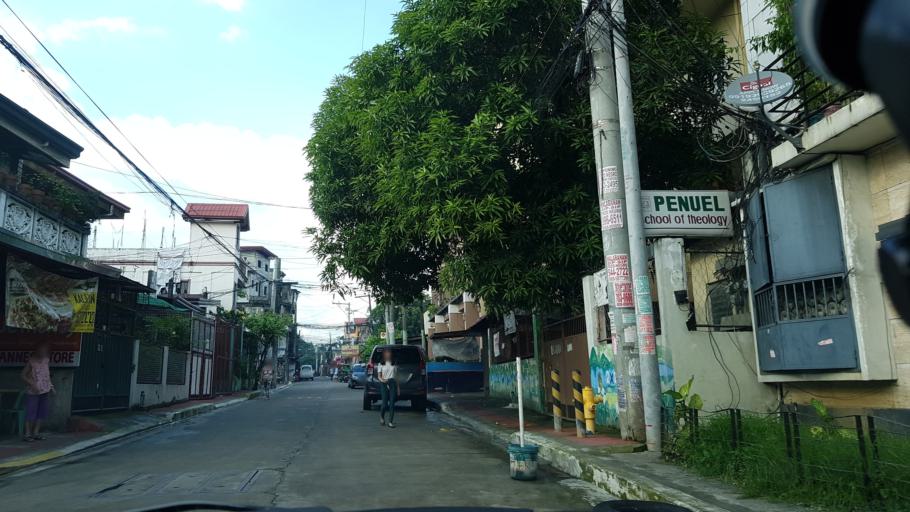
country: PH
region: Metro Manila
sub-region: Quezon City
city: Quezon City
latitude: 14.6381
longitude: 121.0517
